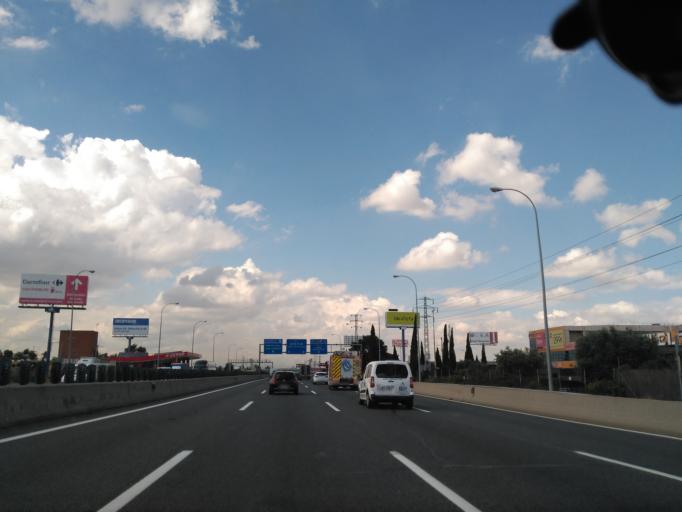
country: ES
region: Madrid
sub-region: Provincia de Madrid
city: Villaverde
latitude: 40.3137
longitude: -3.6919
